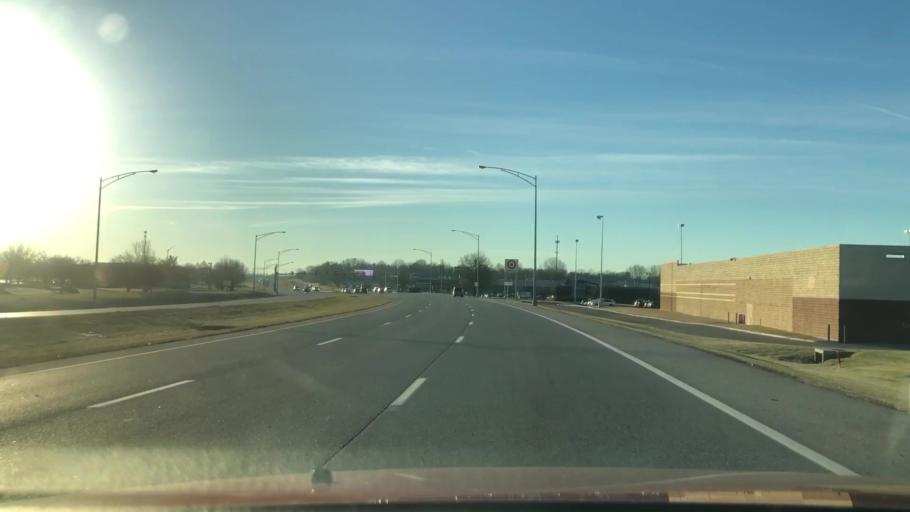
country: US
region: Missouri
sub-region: Greene County
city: Springfield
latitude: 37.1529
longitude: -93.2624
